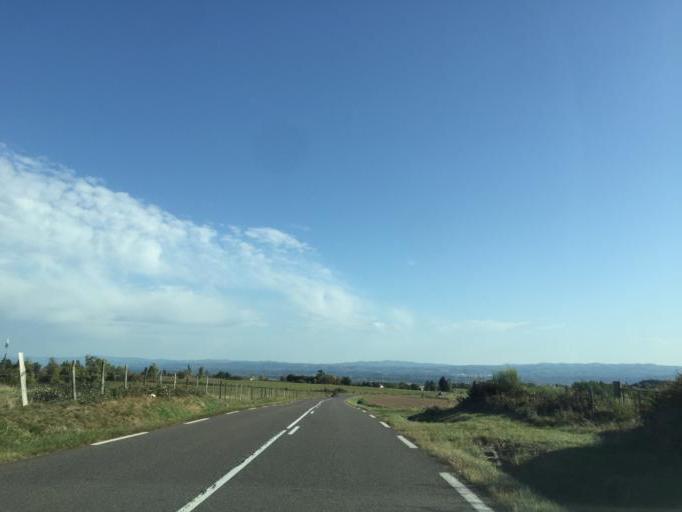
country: FR
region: Rhone-Alpes
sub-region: Departement de la Loire
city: Perigneux
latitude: 45.4717
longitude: 4.1392
